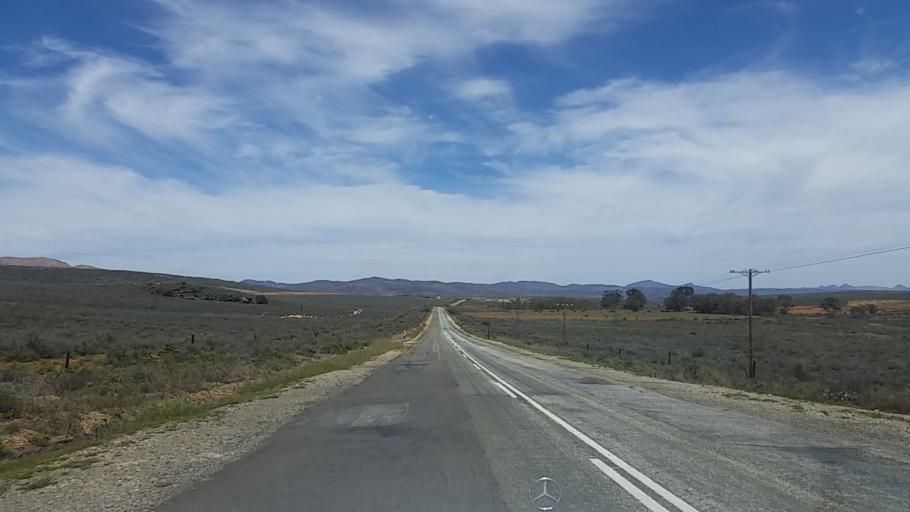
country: ZA
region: Eastern Cape
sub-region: Cacadu District Municipality
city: Willowmore
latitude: -33.5944
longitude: 23.1516
